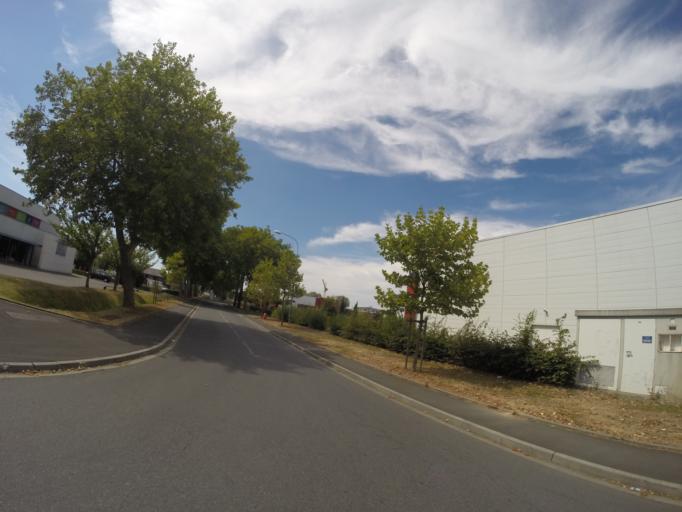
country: FR
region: Centre
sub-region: Departement d'Indre-et-Loire
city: Chanceaux-sur-Choisille
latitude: 47.4313
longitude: 0.7069
